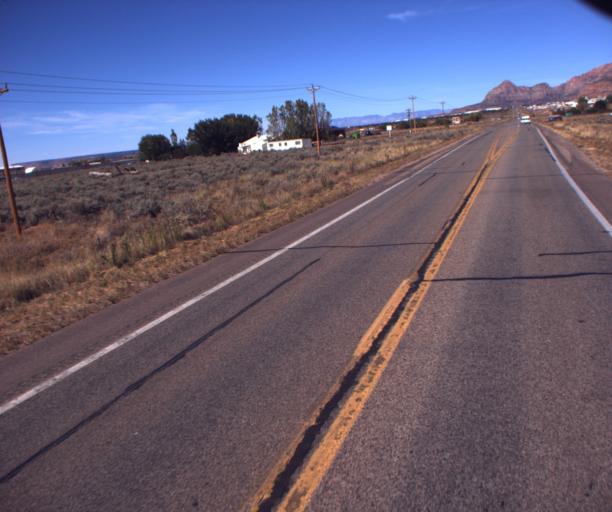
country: US
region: Arizona
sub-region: Mohave County
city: Colorado City
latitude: 36.9817
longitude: -112.9840
